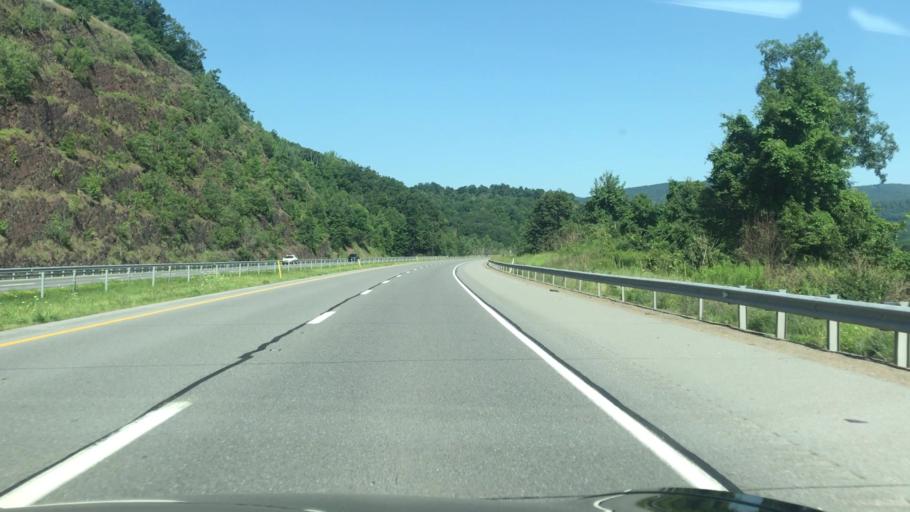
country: US
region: Pennsylvania
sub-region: Lycoming County
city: Garden View
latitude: 41.3092
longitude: -77.0823
